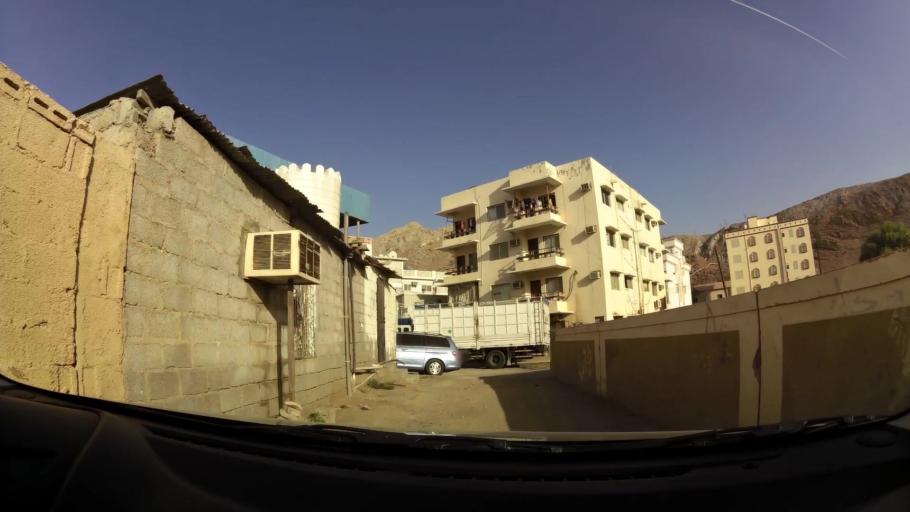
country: OM
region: Muhafazat Masqat
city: Muscat
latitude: 23.5862
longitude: 58.5520
